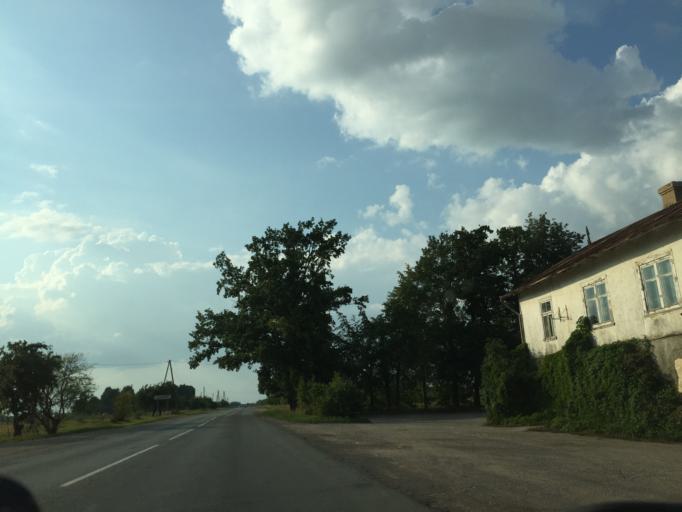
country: LV
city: Tervete
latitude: 56.5193
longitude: 23.3314
